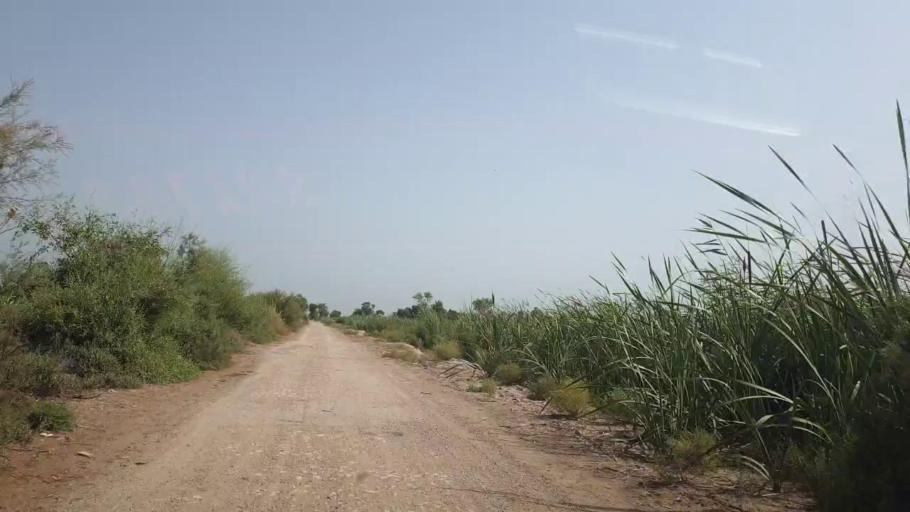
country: PK
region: Sindh
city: Daur
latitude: 26.3111
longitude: 68.2153
